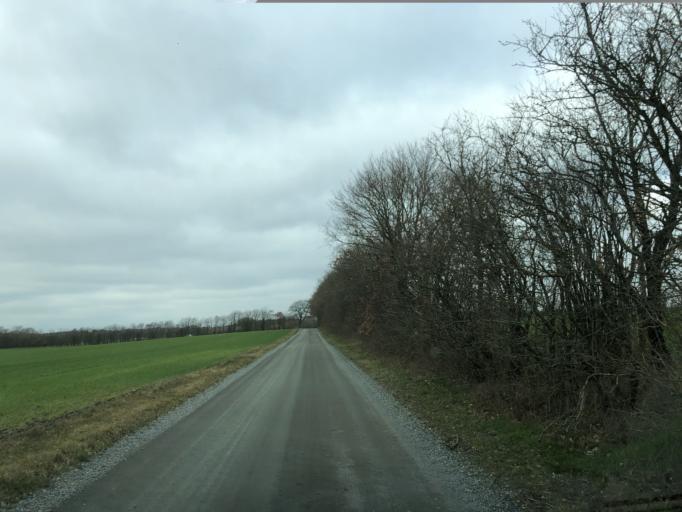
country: DK
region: South Denmark
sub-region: Billund Kommune
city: Billund
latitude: 55.7708
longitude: 9.1441
